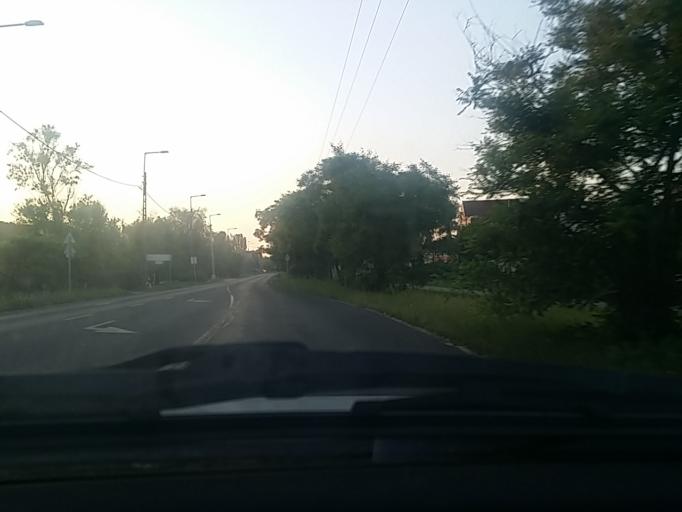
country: HU
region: Budapest
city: Budapest XVII. keruelet
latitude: 47.4734
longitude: 19.2745
